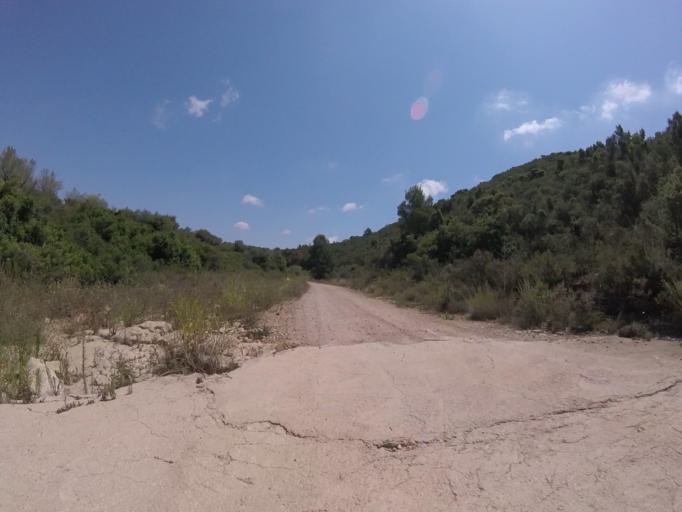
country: ES
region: Valencia
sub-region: Provincia de Castello
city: Torreblanca
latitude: 40.2232
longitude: 0.1531
